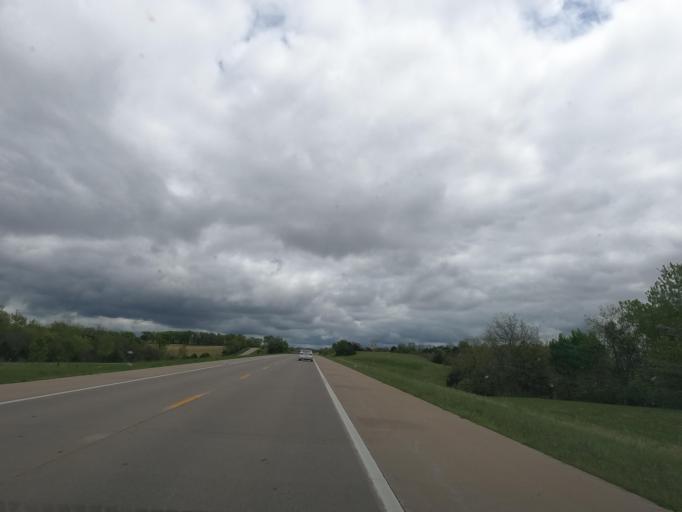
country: US
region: Kansas
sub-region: Wilson County
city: Neodesha
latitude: 37.3551
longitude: -95.6536
